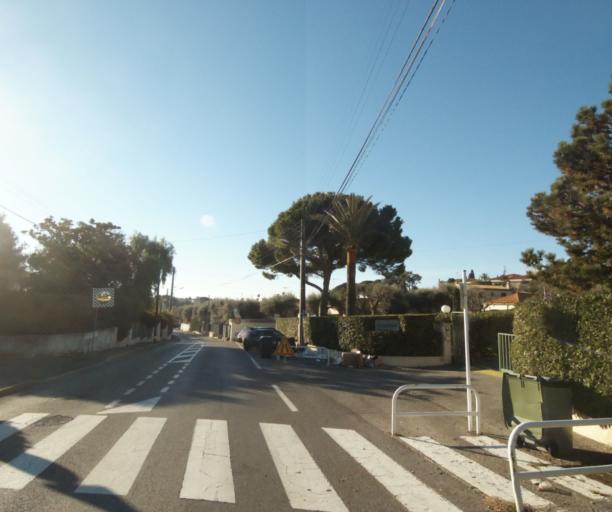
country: FR
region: Provence-Alpes-Cote d'Azur
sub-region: Departement des Alpes-Maritimes
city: Antibes
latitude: 43.5804
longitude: 7.1053
